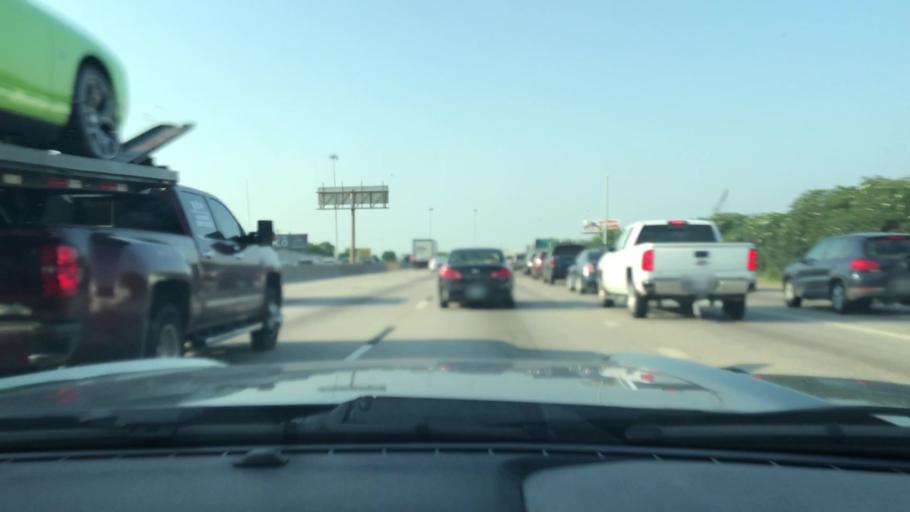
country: US
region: Texas
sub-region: Harris County
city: Jacinto City
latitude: 29.7641
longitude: -95.2652
